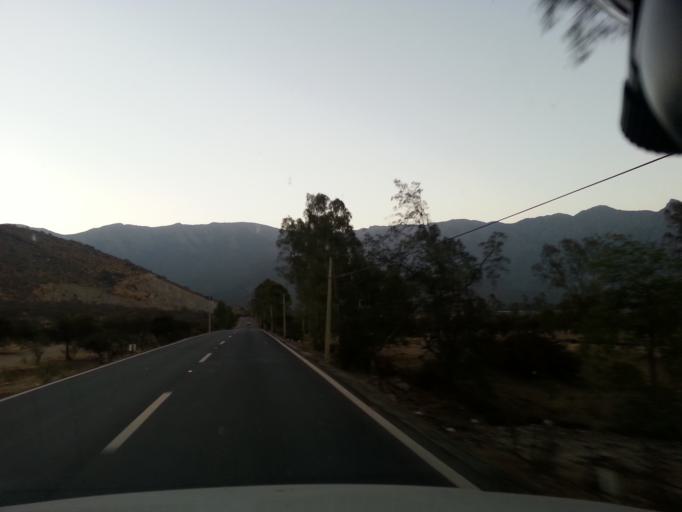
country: CL
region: Santiago Metropolitan
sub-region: Provincia de Chacabuco
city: Lampa
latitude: -33.2460
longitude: -70.9159
